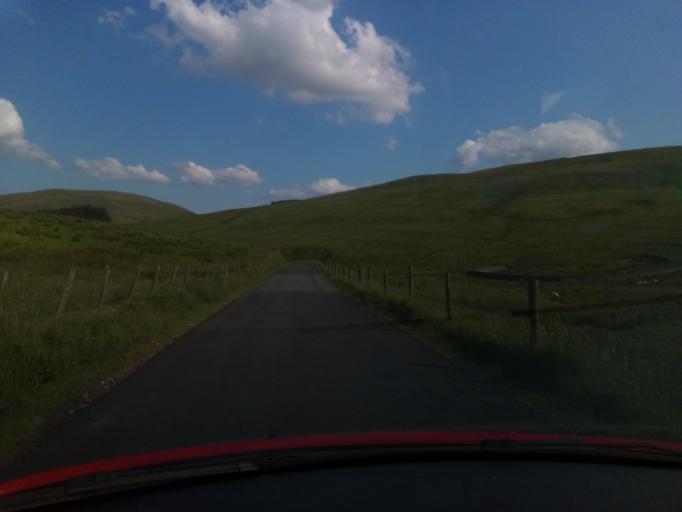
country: GB
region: Scotland
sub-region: The Scottish Borders
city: Innerleithen
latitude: 55.4568
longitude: -3.1122
